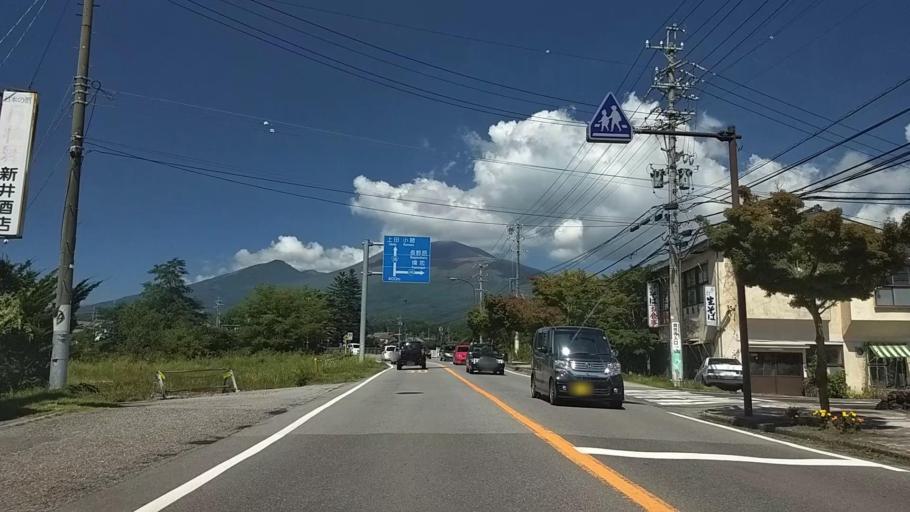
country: JP
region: Nagano
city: Komoro
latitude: 36.3481
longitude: 138.5965
